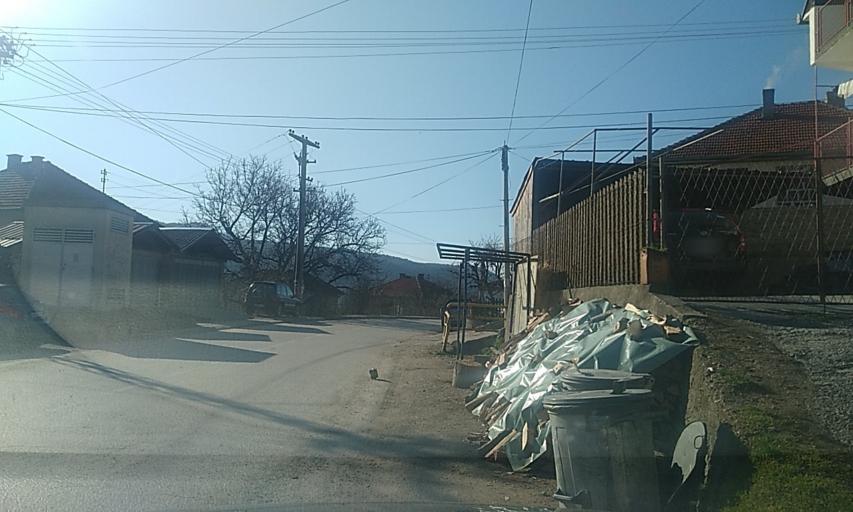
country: RS
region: Central Serbia
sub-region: Pcinjski Okrug
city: Bosilegrad
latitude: 42.4900
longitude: 22.4713
